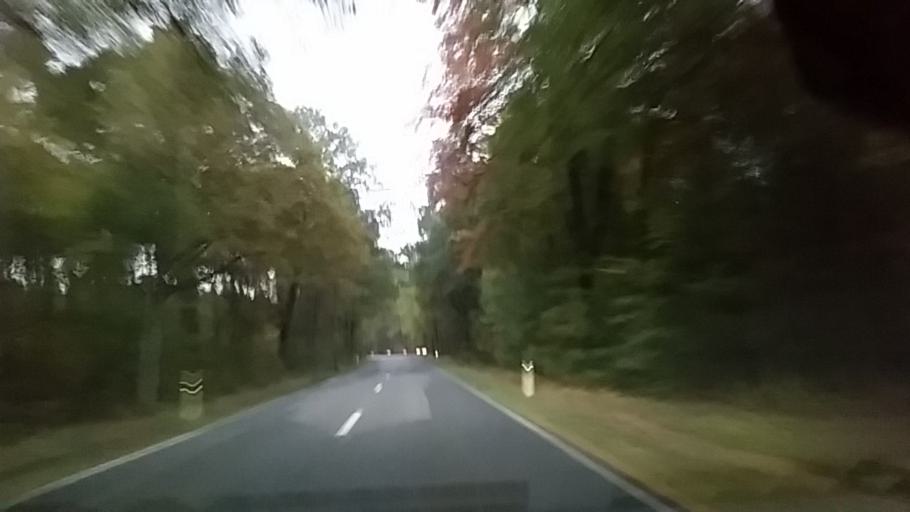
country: DE
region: Lower Saxony
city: Tulau
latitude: 52.6342
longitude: 10.8107
